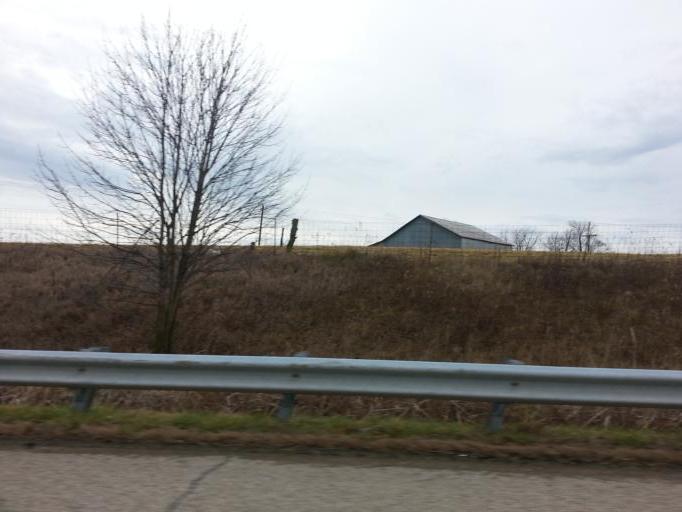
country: US
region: Indiana
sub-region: Decatur County
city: Greensburg
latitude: 39.3387
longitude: -85.4128
